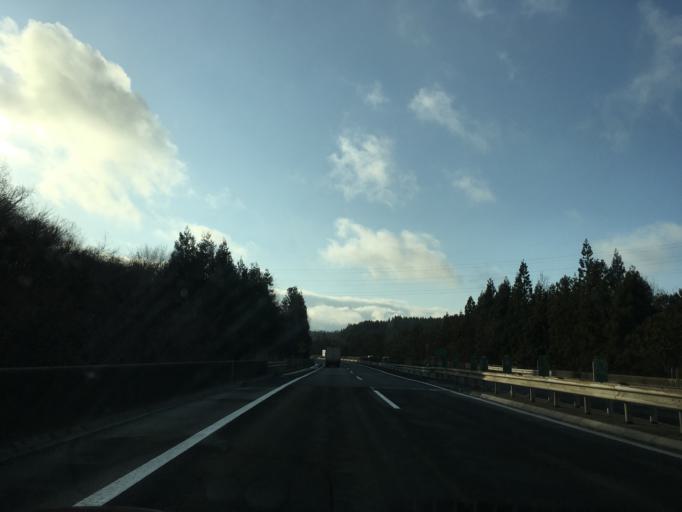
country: JP
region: Miyagi
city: Okawara
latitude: 38.1570
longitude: 140.6876
